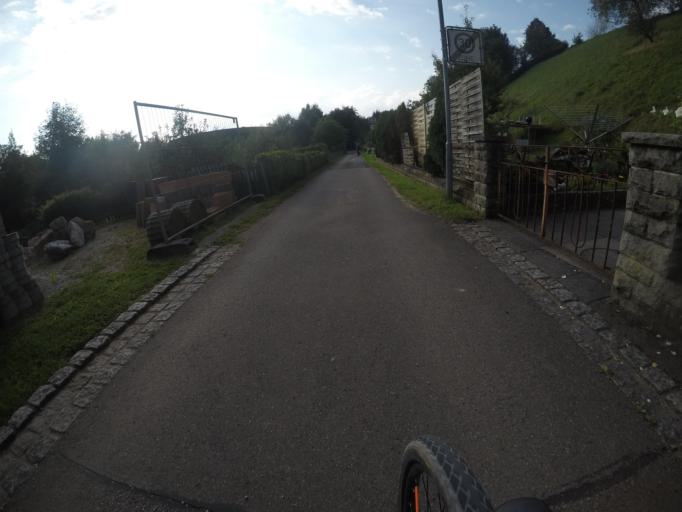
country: DE
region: Baden-Wuerttemberg
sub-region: Regierungsbezirk Stuttgart
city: Neckartenzlingen
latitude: 48.5863
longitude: 9.2406
